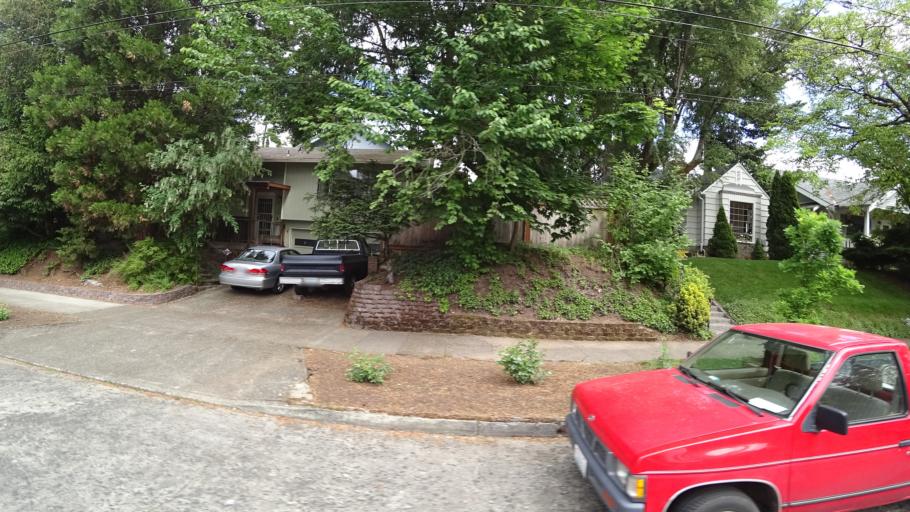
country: US
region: Oregon
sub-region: Multnomah County
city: Lents
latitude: 45.5078
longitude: -122.6071
